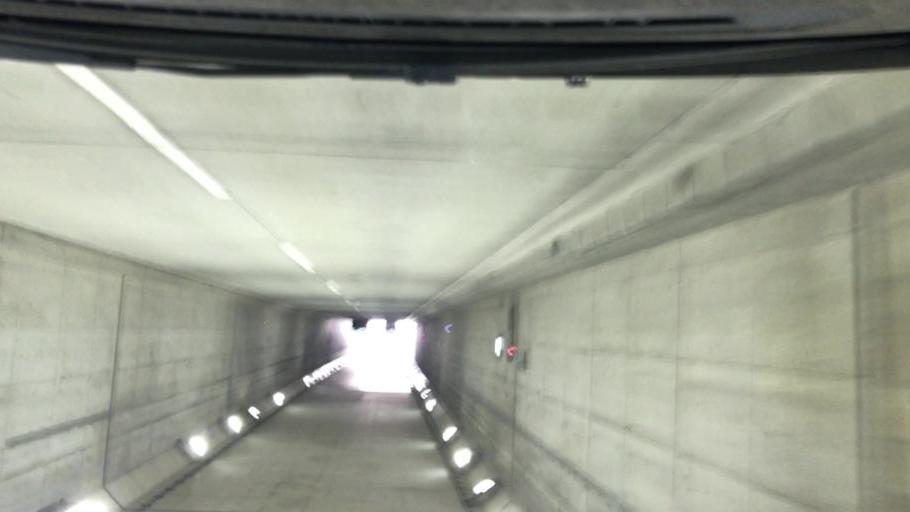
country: JP
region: Hyogo
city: Takarazuka
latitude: 34.8291
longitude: 135.2959
